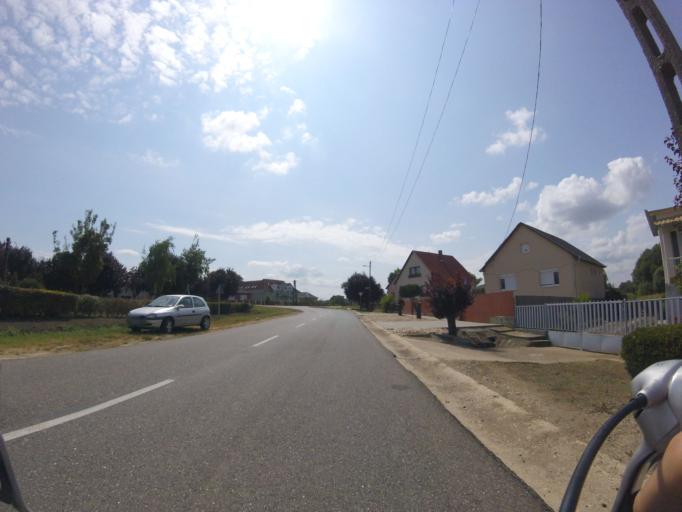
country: HU
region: Szabolcs-Szatmar-Bereg
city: Nyirbogdany
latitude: 48.0482
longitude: 21.8700
